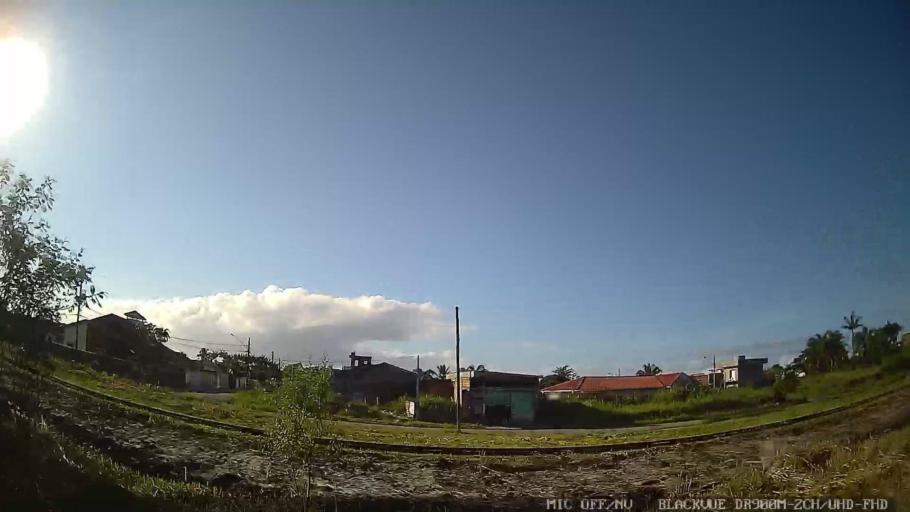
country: BR
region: Sao Paulo
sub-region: Peruibe
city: Peruibe
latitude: -24.2768
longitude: -46.9547
